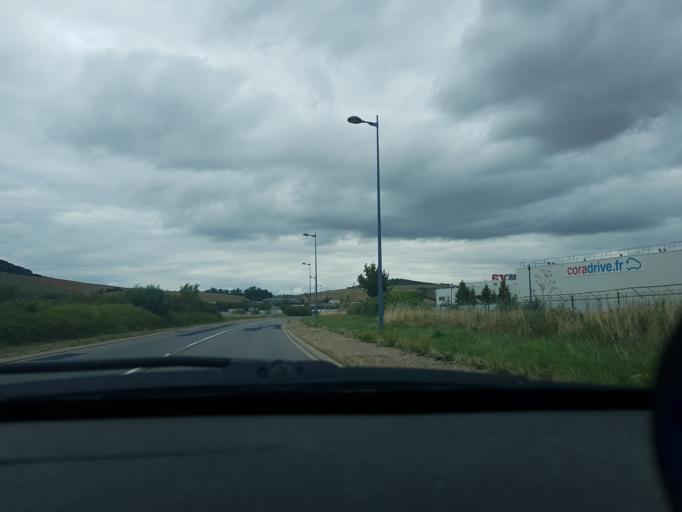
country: FR
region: Lorraine
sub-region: Departement de Meurthe-et-Moselle
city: Saulxures-les-Nancy
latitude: 48.7031
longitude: 6.2421
